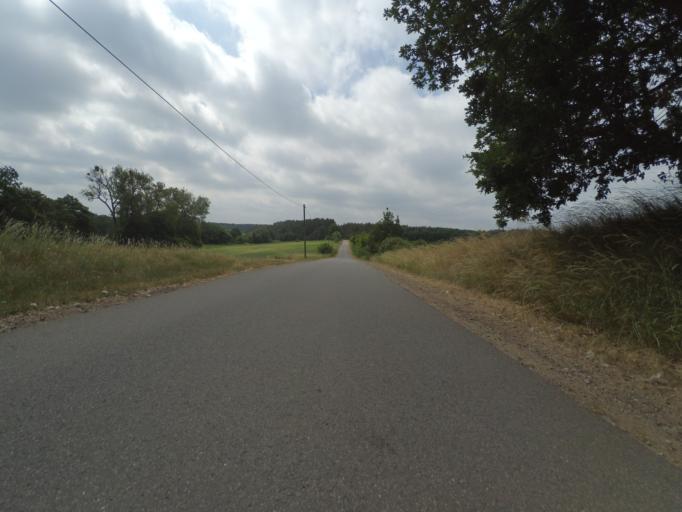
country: DE
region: Mecklenburg-Vorpommern
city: Krakow am See
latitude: 53.6023
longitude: 12.3845
